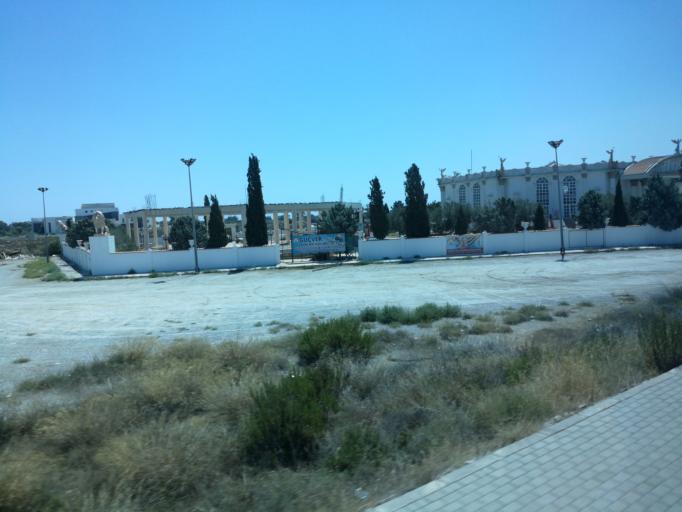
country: CY
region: Ammochostos
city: Famagusta
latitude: 35.1642
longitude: 33.9003
